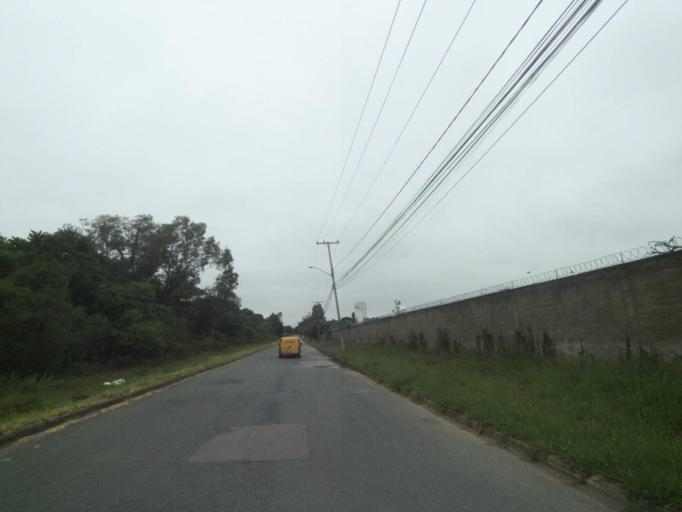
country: BR
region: Parana
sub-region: Araucaria
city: Araucaria
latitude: -25.5398
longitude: -49.3271
